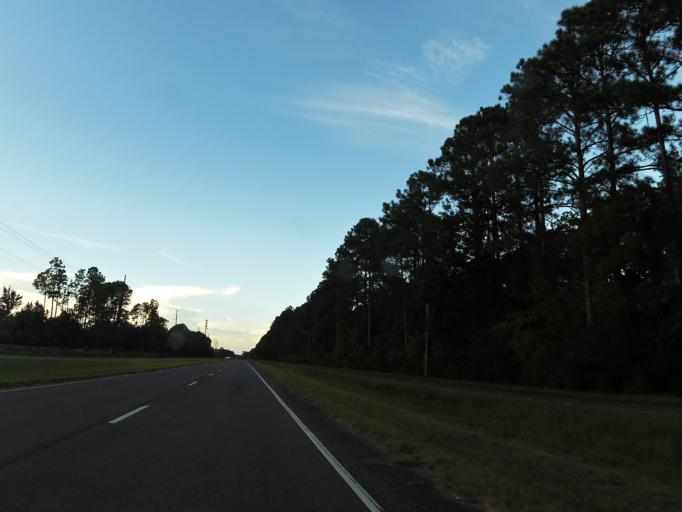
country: US
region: Georgia
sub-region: Camden County
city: St Marys
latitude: 30.7746
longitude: -81.5764
